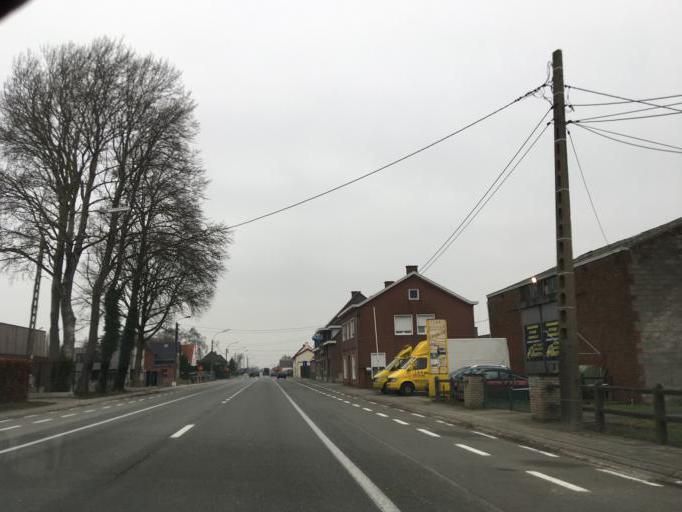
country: BE
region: Flanders
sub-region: Provincie West-Vlaanderen
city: Pittem
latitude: 50.9635
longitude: 3.2441
